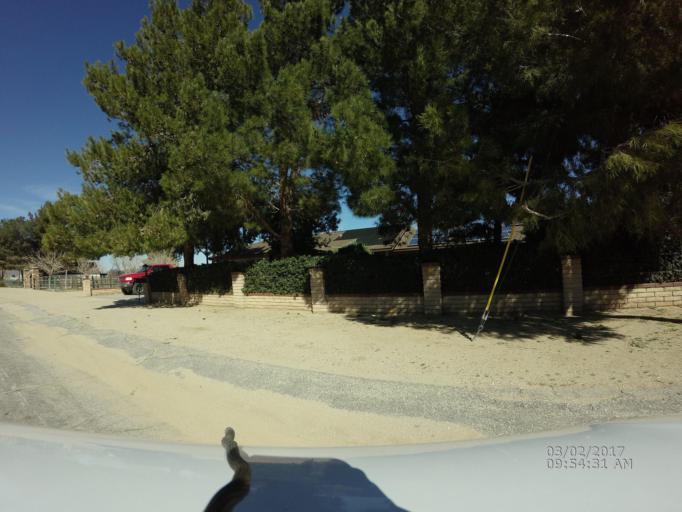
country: US
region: California
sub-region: Los Angeles County
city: Quartz Hill
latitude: 34.6401
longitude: -118.2145
